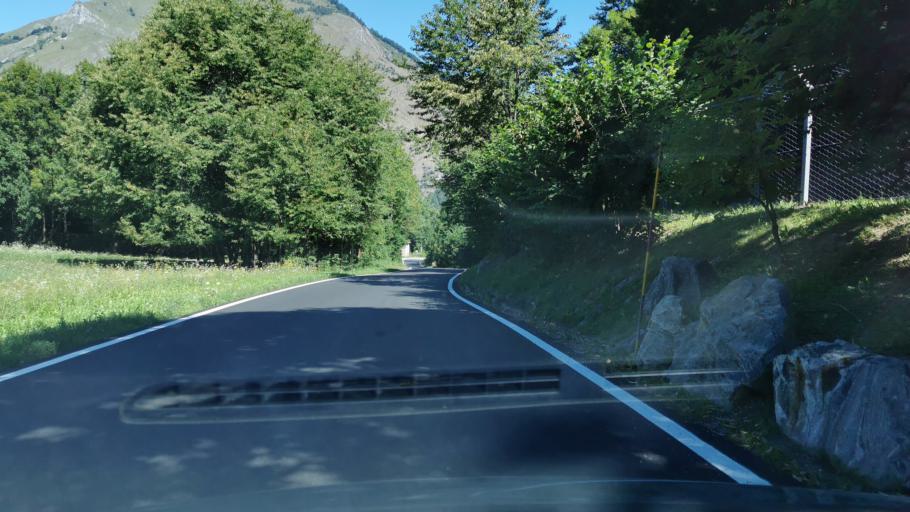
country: IT
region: Piedmont
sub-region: Provincia di Cuneo
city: Entracque
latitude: 44.2511
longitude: 7.3840
